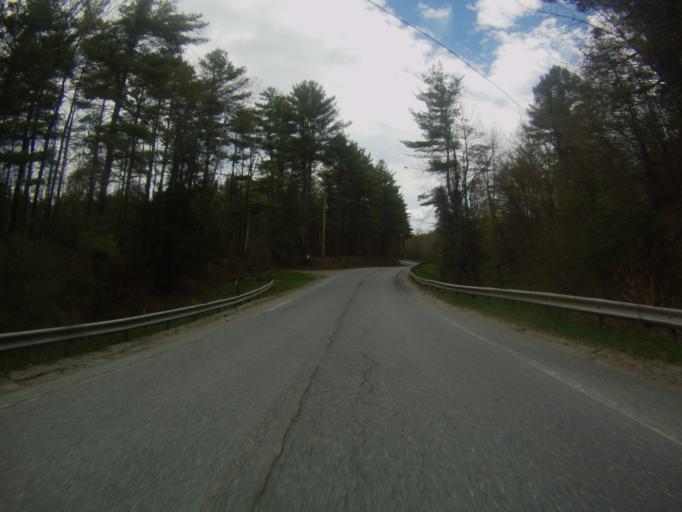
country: US
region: New York
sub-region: Essex County
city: Mineville
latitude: 44.0910
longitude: -73.5486
